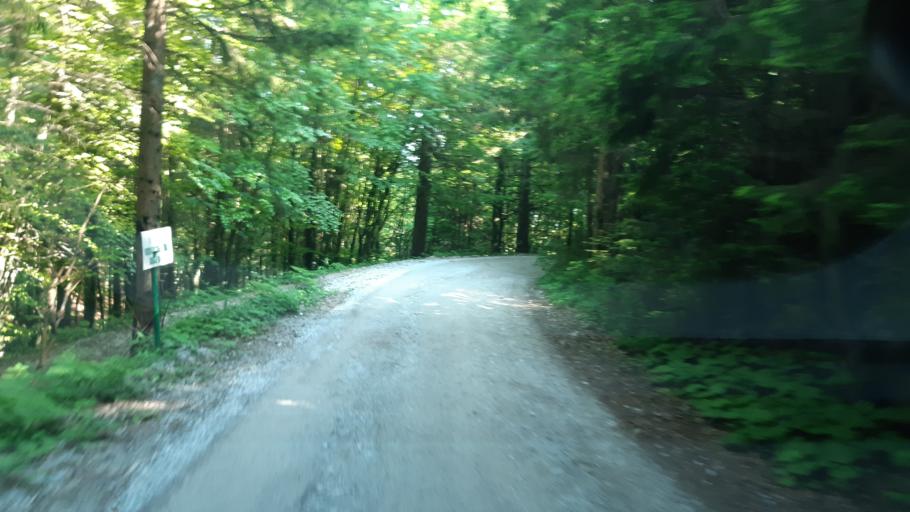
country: SI
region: Trzic
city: Bistrica pri Trzicu
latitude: 46.3687
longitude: 14.2777
